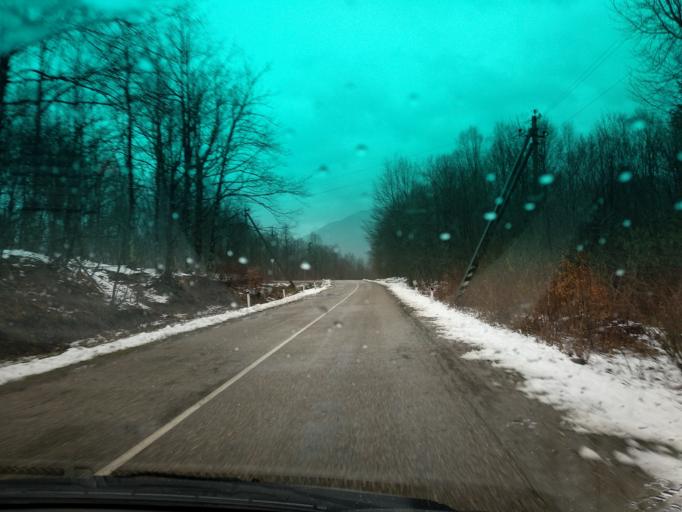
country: RU
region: Krasnodarskiy
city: Khadyzhensk
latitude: 44.2068
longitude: 39.3981
